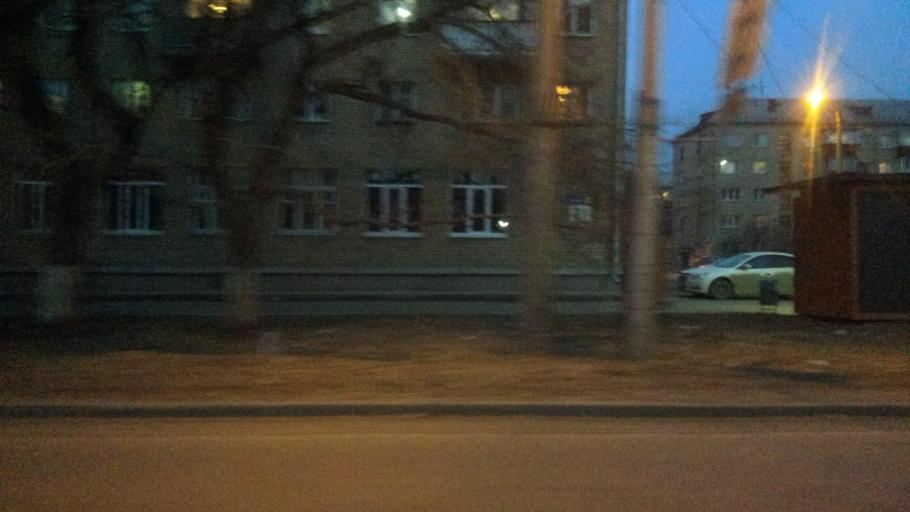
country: RU
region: Chelyabinsk
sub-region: Gorod Chelyabinsk
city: Chelyabinsk
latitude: 55.1674
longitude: 61.4601
